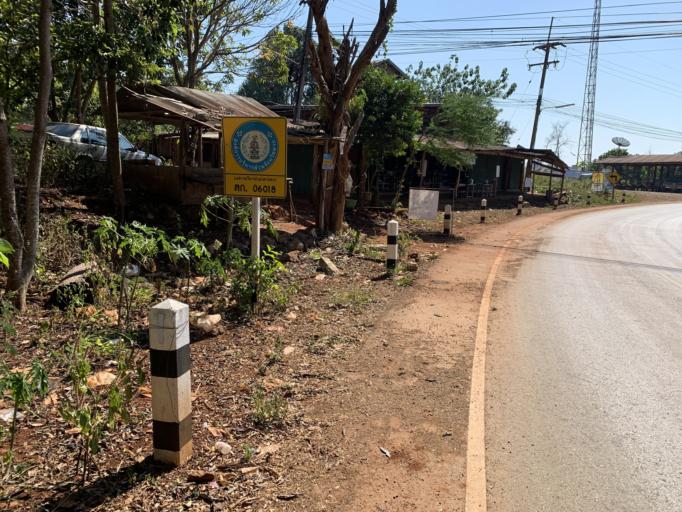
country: TH
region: Tak
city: Phop Phra
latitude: 16.4856
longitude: 98.7625
